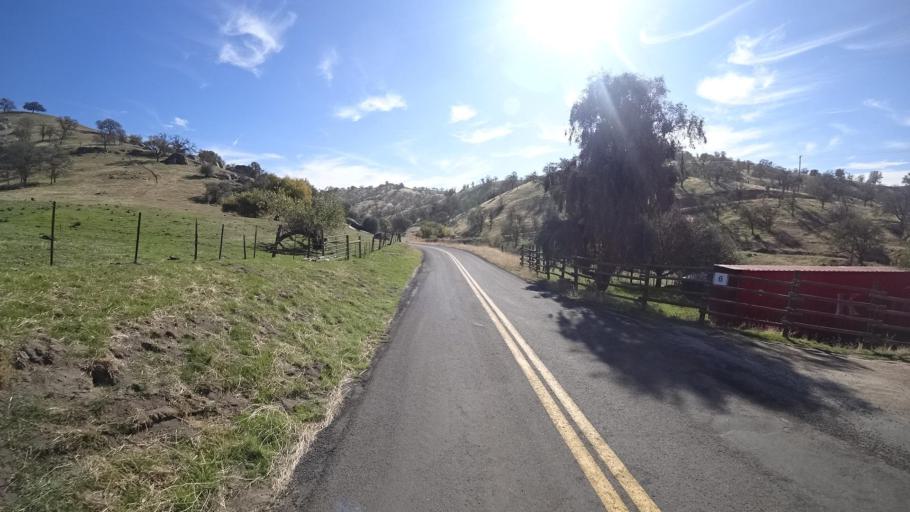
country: US
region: California
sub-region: Kern County
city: Oildale
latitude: 35.6563
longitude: -118.8419
